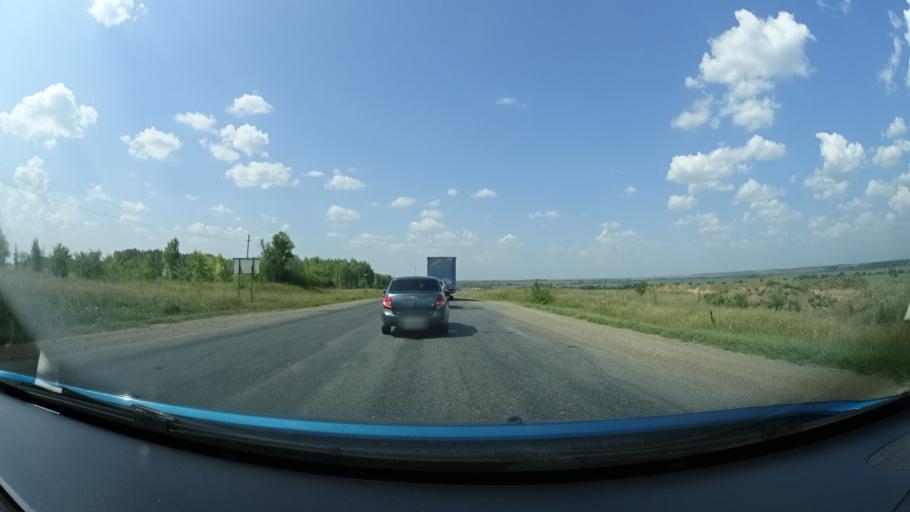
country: RU
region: Bashkortostan
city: Buzdyak
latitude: 54.6608
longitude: 54.6913
